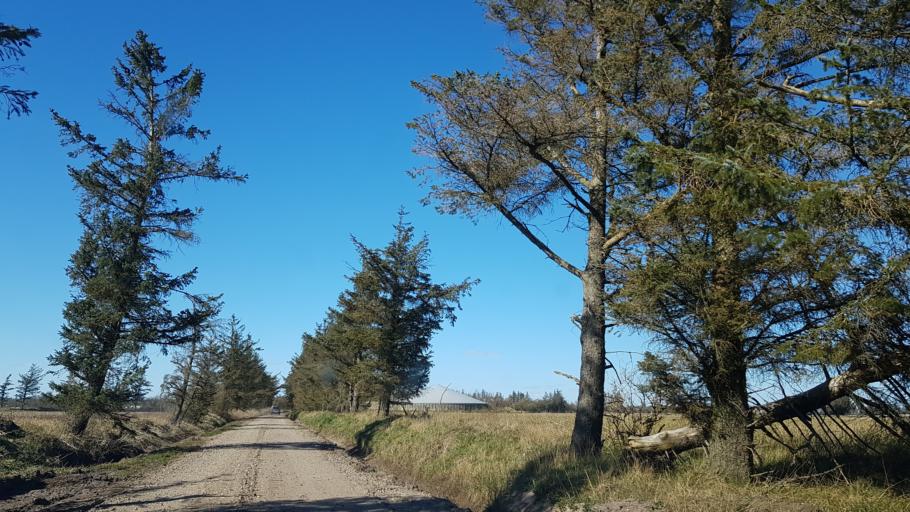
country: DK
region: South Denmark
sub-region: Esbjerg Kommune
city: Ribe
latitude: 55.2466
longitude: 8.7118
